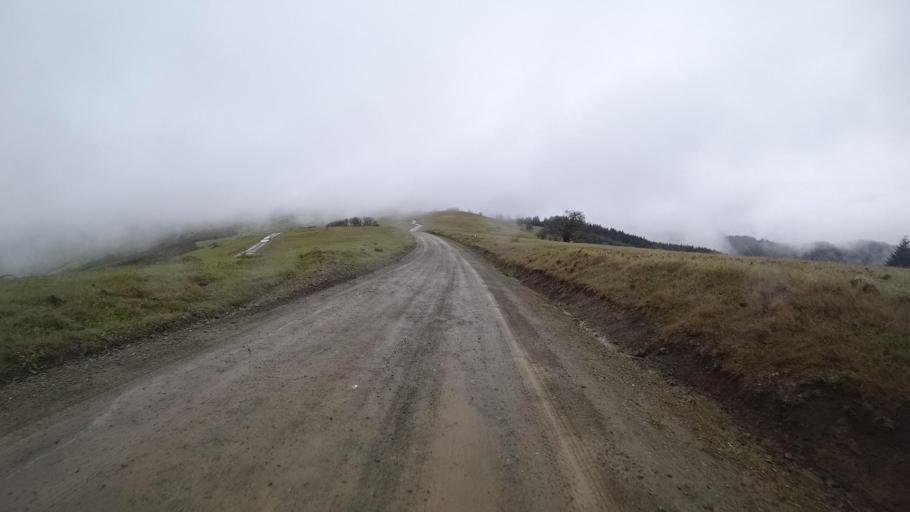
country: US
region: California
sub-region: Humboldt County
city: Westhaven-Moonstone
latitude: 41.1416
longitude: -123.8634
